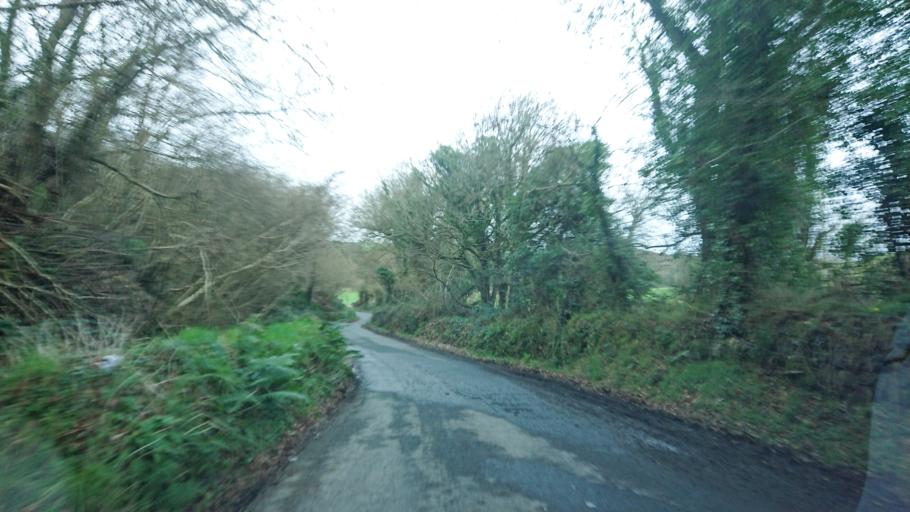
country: IE
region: Munster
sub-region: Waterford
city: Tra Mhor
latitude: 52.1538
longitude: -7.2589
